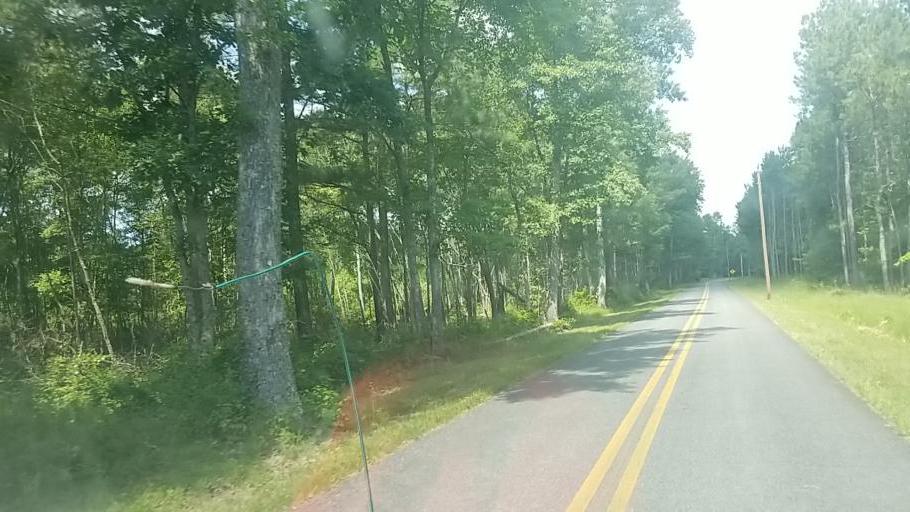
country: US
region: Maryland
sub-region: Worcester County
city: Snow Hill
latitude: 38.2532
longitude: -75.4352
